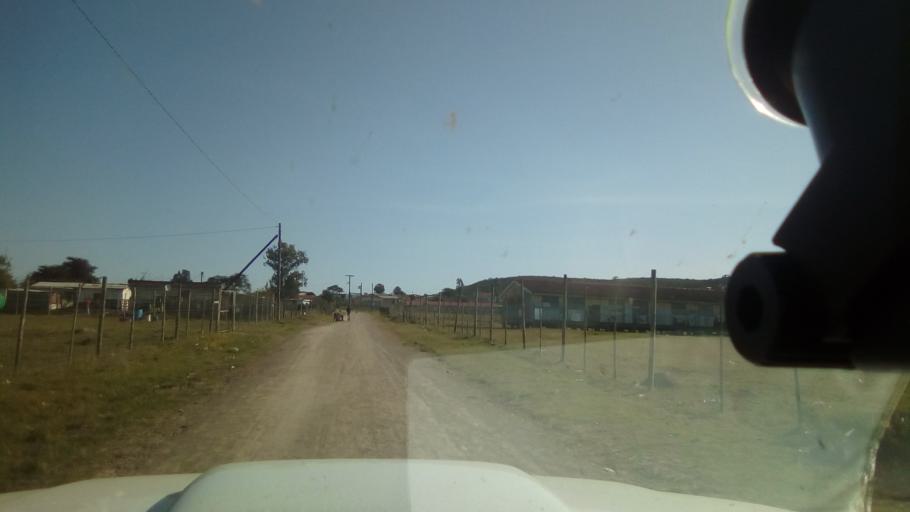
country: ZA
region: Eastern Cape
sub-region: Buffalo City Metropolitan Municipality
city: Bhisho
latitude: -32.8159
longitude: 27.3563
